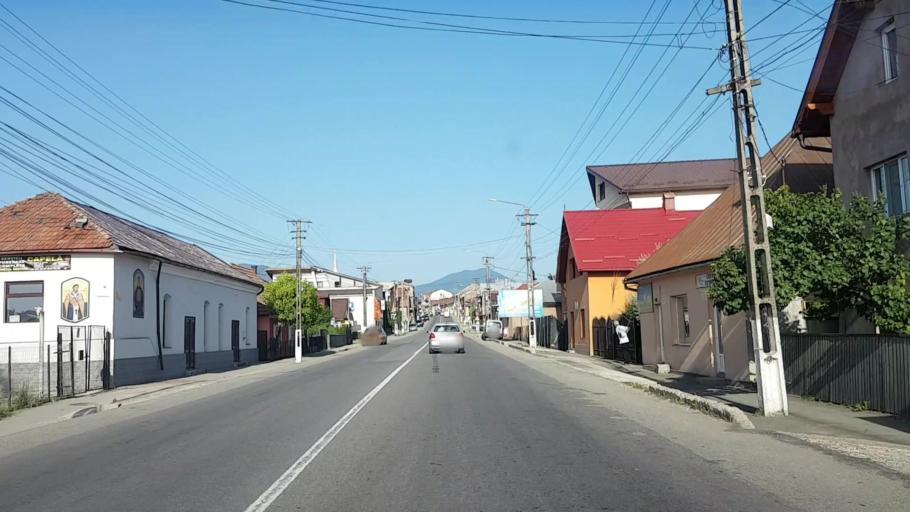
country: RO
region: Bistrita-Nasaud
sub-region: Comuna Prundu Bargaului
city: Susenii Bargaului
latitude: 47.2199
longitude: 24.7342
